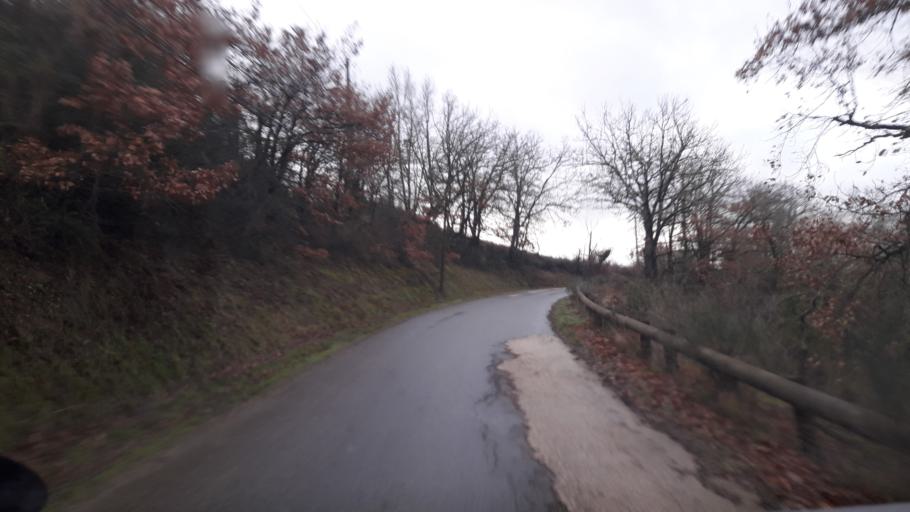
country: FR
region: Midi-Pyrenees
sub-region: Departement de la Haute-Garonne
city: Marquefave
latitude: 43.3130
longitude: 1.2443
